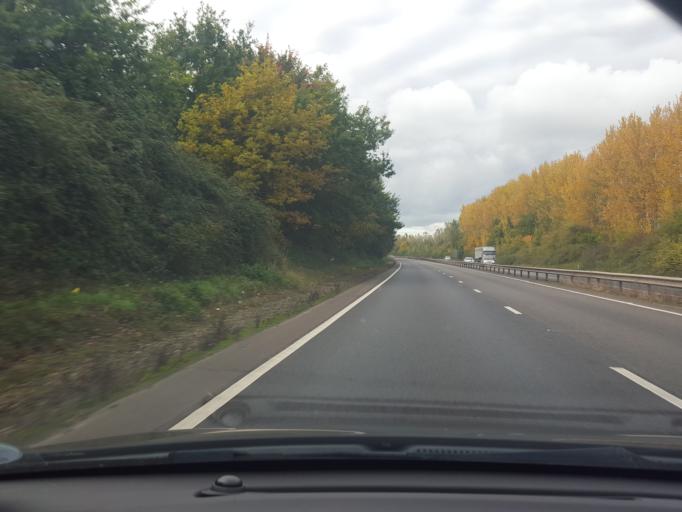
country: GB
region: England
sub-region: Suffolk
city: Thurston
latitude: 52.2354
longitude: 0.8394
